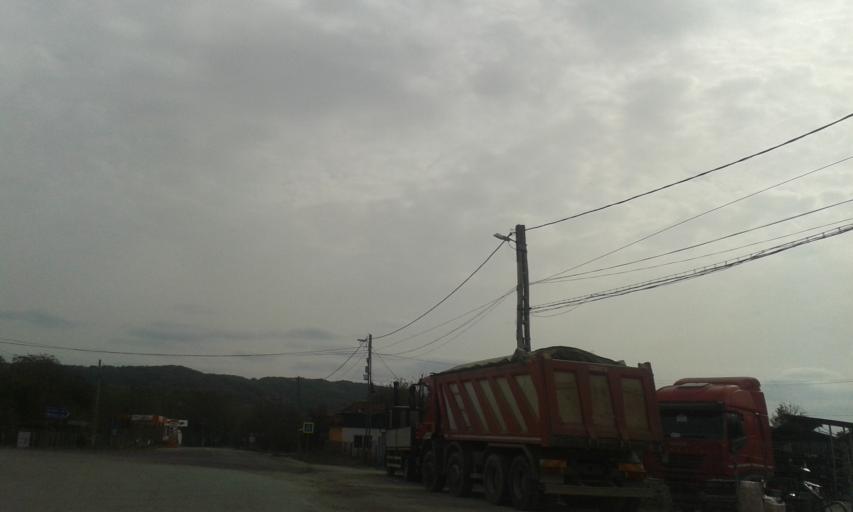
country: RO
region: Gorj
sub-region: Comuna Hurezani
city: Hurezani
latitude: 44.8169
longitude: 23.6531
